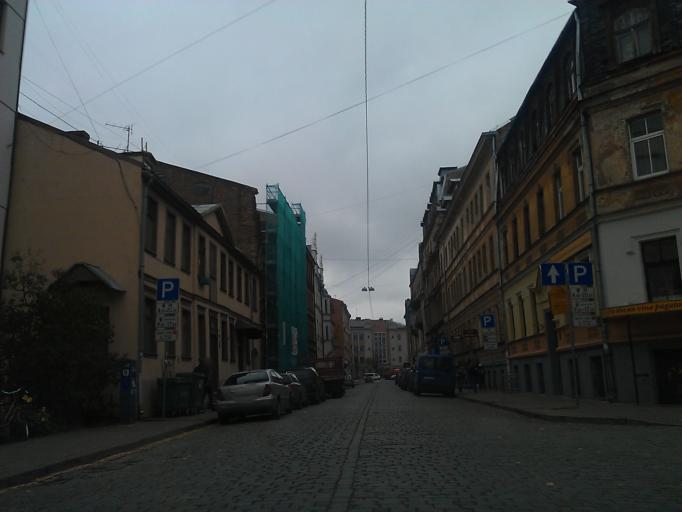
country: LV
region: Riga
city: Riga
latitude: 56.9609
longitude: 24.1083
